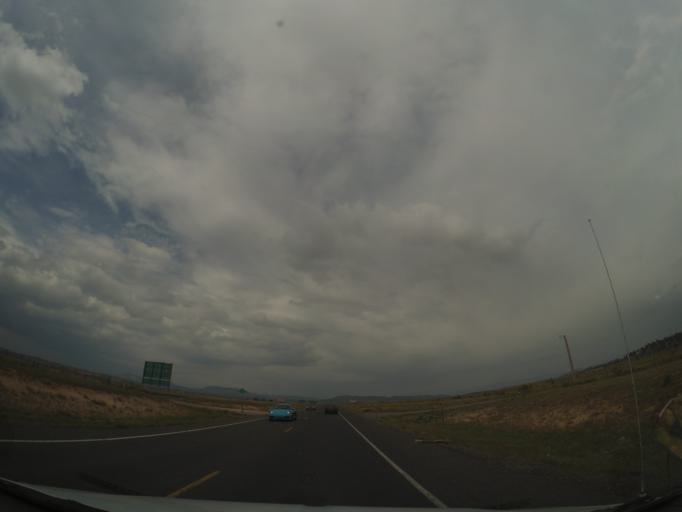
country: US
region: Utah
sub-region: Garfield County
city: Panguitch
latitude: 37.6804
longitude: -112.1547
